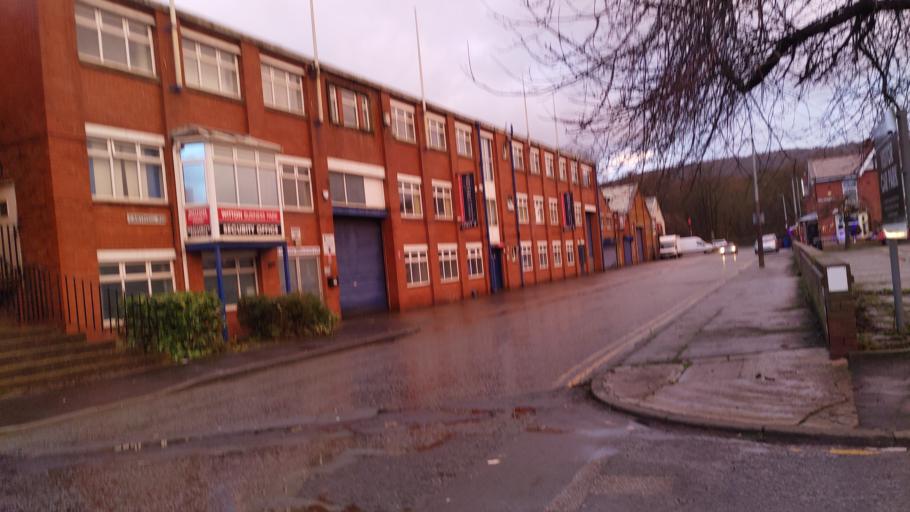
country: GB
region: England
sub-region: Blackburn with Darwen
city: Blackburn
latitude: 53.7383
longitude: -2.5094
